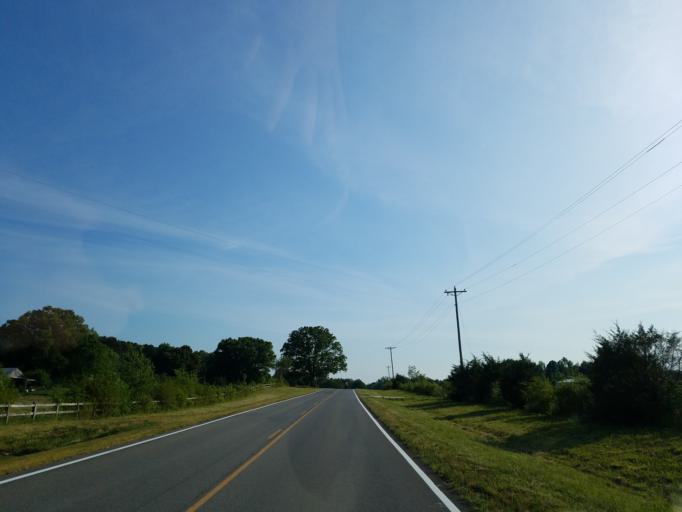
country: US
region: Georgia
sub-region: Chattooga County
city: Trion
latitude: 34.5351
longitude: -85.2080
